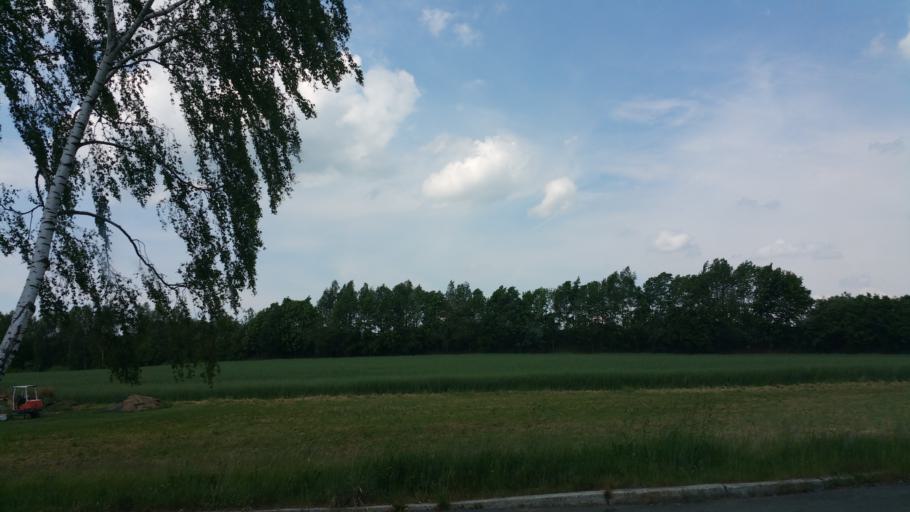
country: DE
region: Bavaria
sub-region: Upper Franconia
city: Schwarzenbach an der Saale
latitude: 50.2258
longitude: 11.9253
